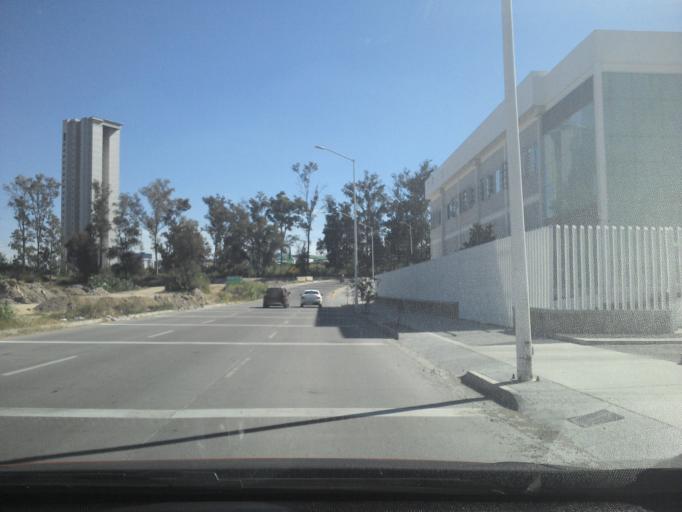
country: MX
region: Jalisco
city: Zapopan2
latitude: 20.7201
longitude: -103.4265
